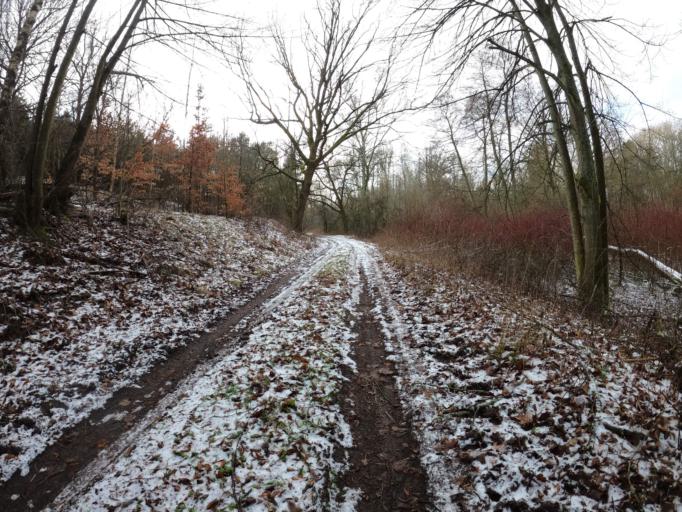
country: PL
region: Lubusz
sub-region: Powiat slubicki
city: Rzepin
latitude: 52.2757
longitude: 14.7936
